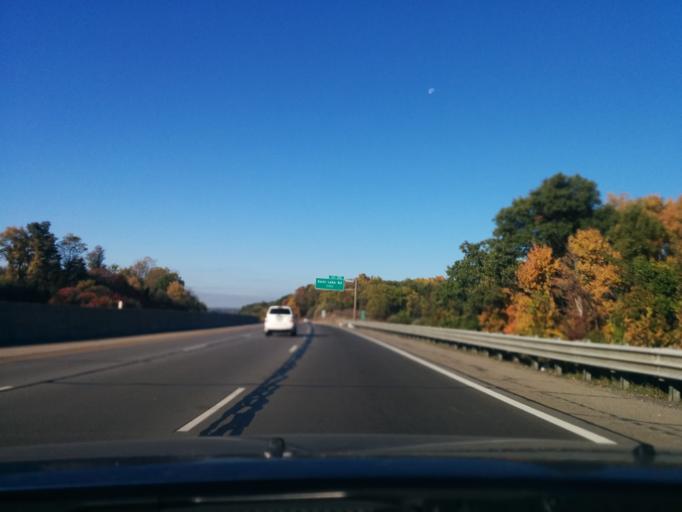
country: US
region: Michigan
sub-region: Oakland County
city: South Lyon
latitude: 42.5214
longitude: -83.6300
